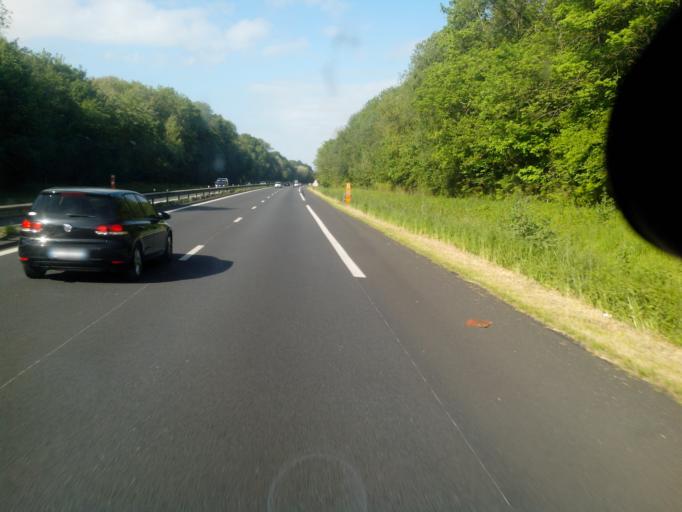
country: FR
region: Lower Normandy
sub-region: Departement du Calvados
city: Troarn
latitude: 49.1924
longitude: -0.1875
